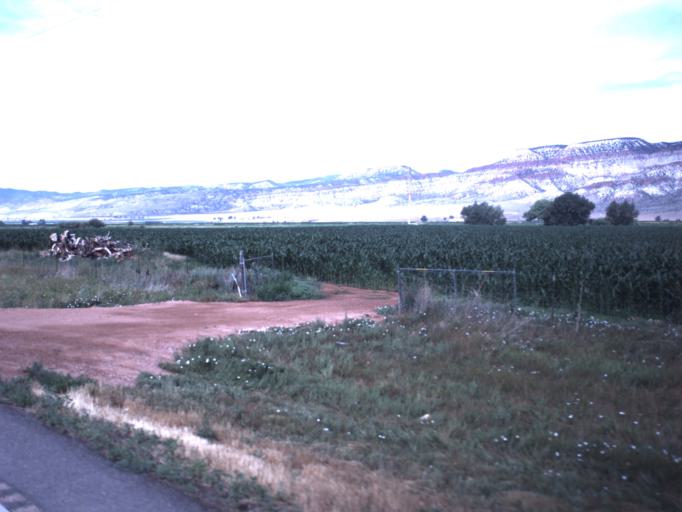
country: US
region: Utah
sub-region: Sevier County
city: Richfield
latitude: 38.8281
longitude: -111.9931
